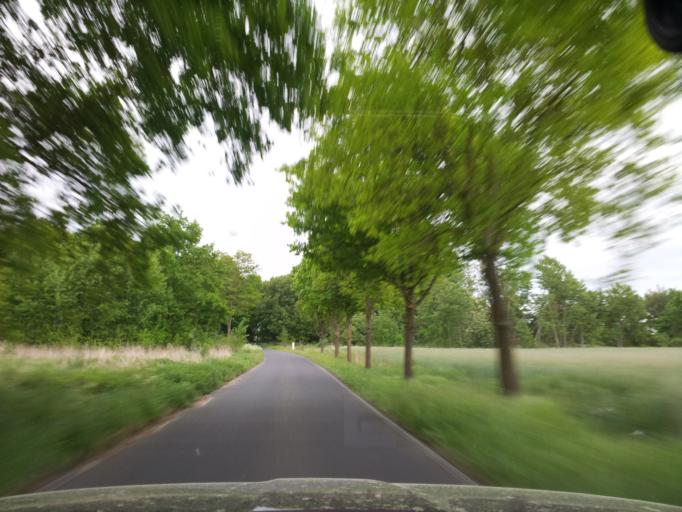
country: DE
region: Brandenburg
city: Niedergorsdorf
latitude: 52.0011
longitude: 12.9562
